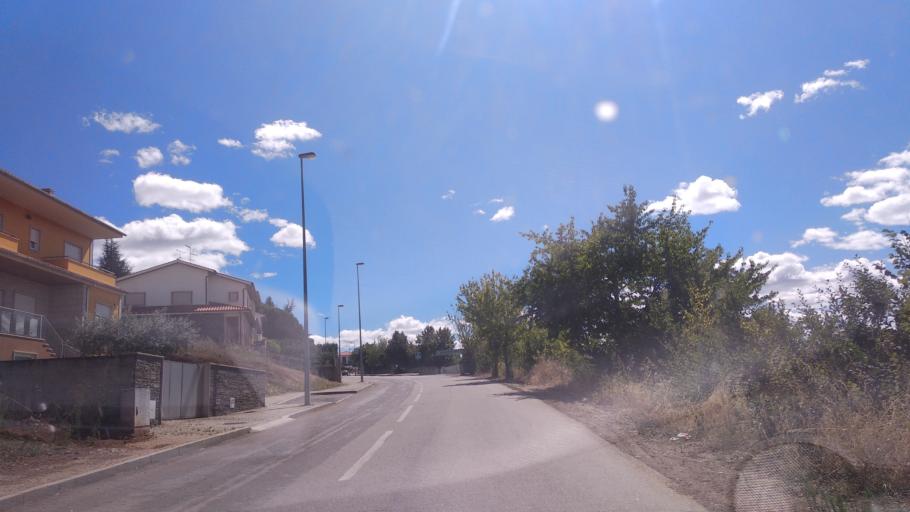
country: PT
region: Braganca
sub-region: Braganca Municipality
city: Braganca
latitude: 41.7907
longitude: -6.7673
